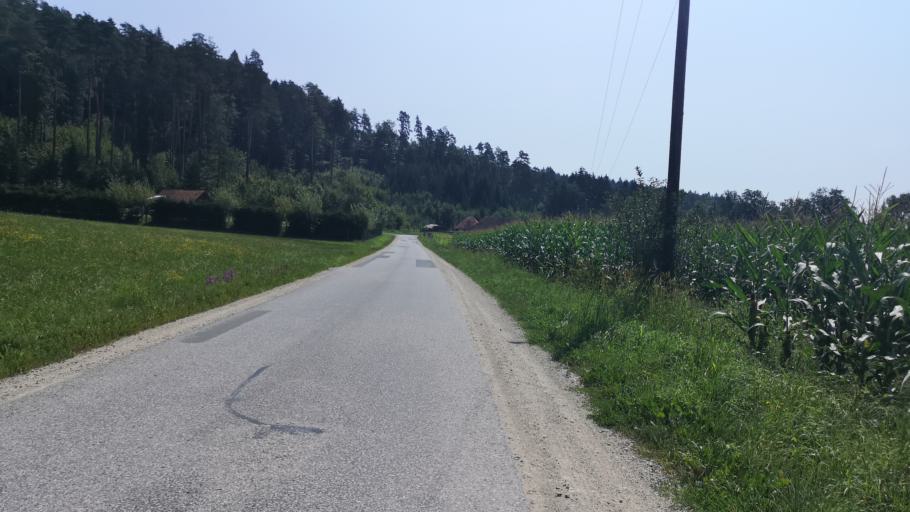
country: AT
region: Styria
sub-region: Politischer Bezirk Deutschlandsberg
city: Sankt Josef (Weststeiermark)
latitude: 46.8895
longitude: 15.3689
